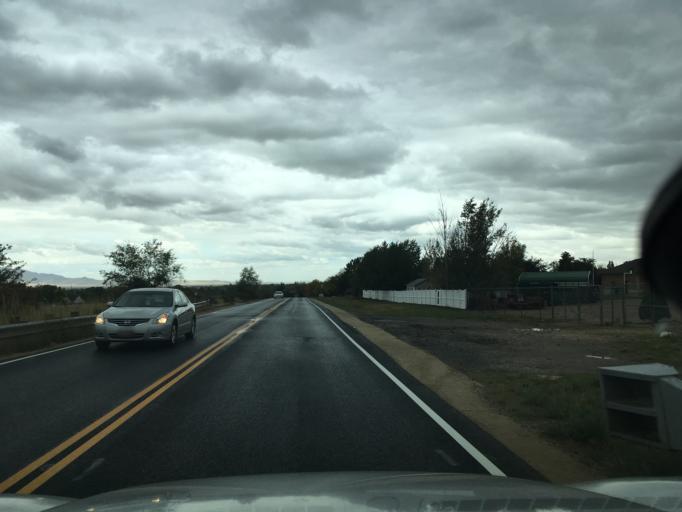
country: US
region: Utah
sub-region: Davis County
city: Kaysville
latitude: 41.0626
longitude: -111.9356
